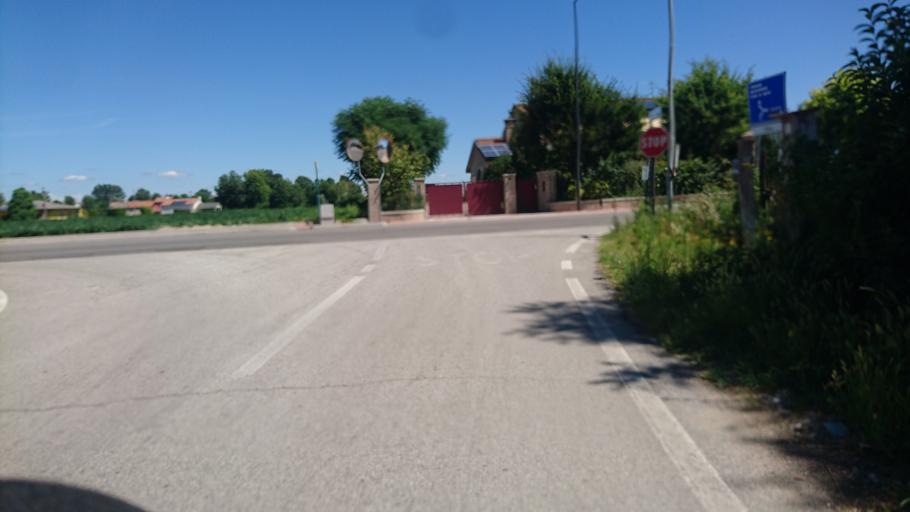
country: IT
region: Veneto
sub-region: Provincia di Padova
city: Campagnola
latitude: 45.2754
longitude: 12.0091
